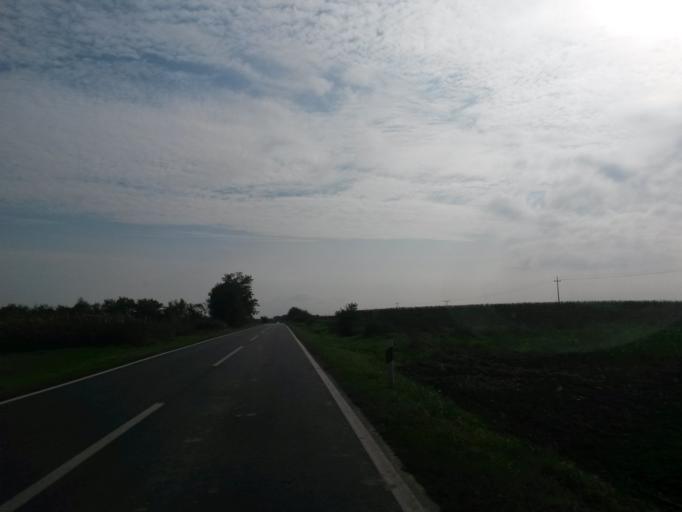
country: HR
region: Vukovarsko-Srijemska
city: Bapska
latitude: 45.2344
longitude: 19.2615
